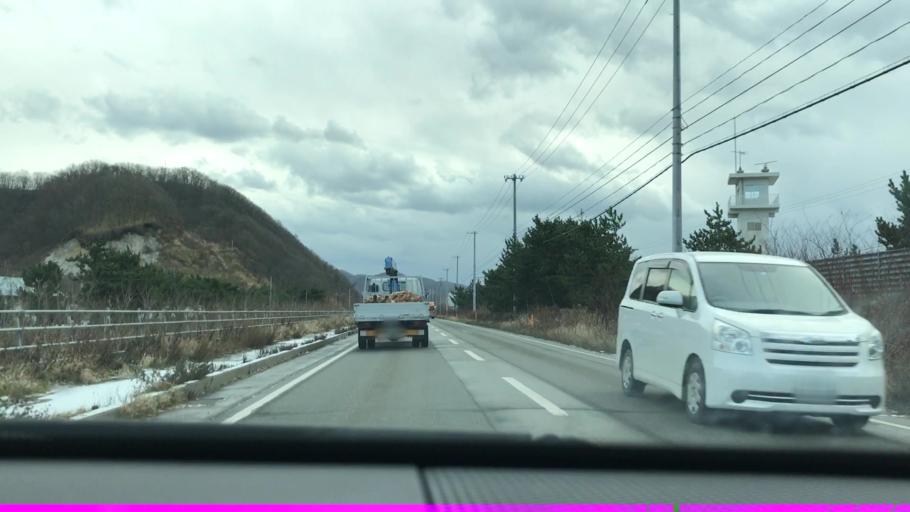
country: JP
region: Hokkaido
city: Shizunai-furukawacho
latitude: 42.3076
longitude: 142.4401
